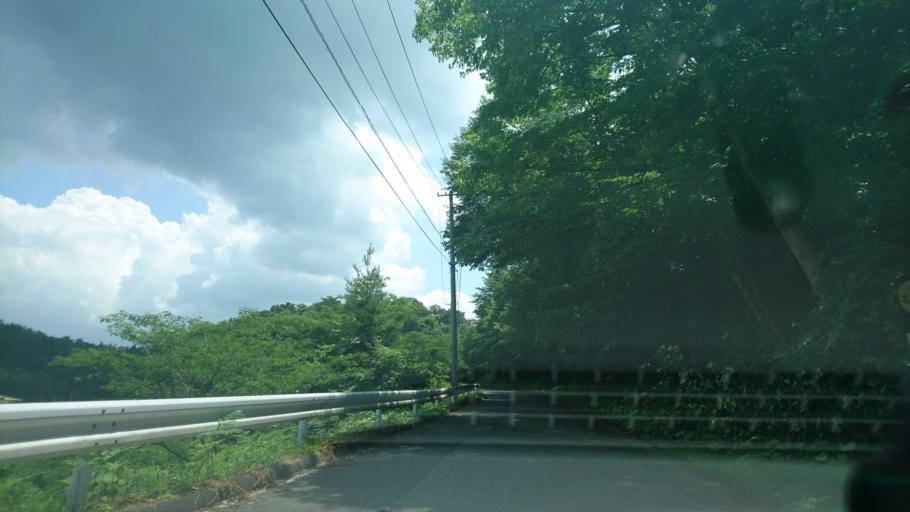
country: JP
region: Iwate
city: Ichinoseki
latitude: 38.9189
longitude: 141.2211
